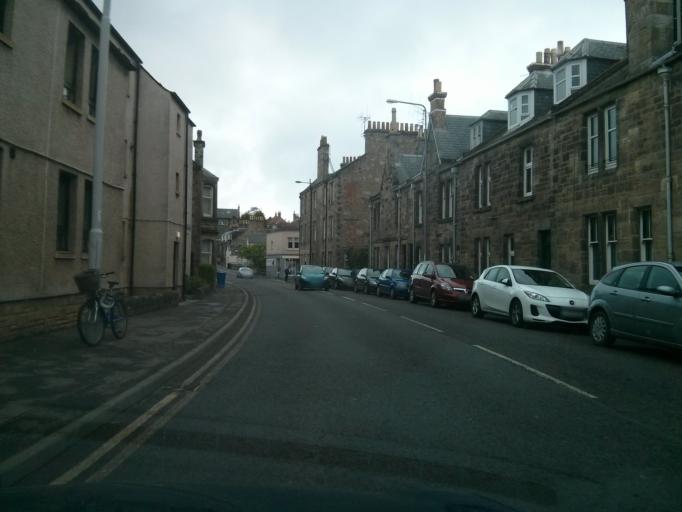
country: GB
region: Scotland
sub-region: Fife
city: Saint Andrews
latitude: 56.3357
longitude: -2.8003
